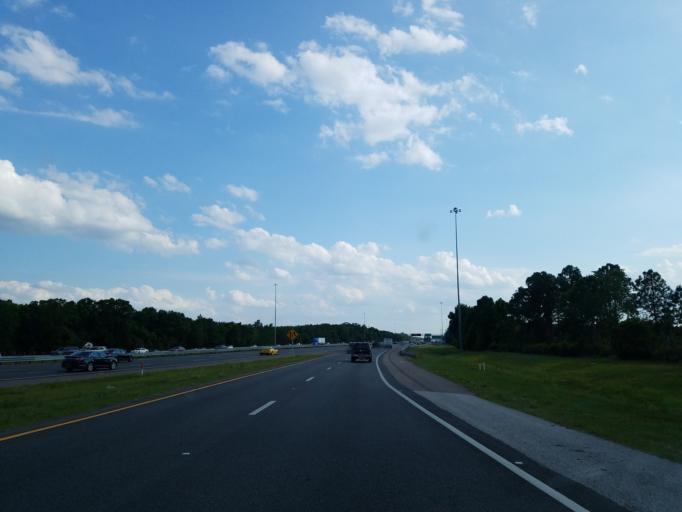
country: US
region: Florida
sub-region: Hillsborough County
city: Pebble Creek
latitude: 28.1916
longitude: -82.3860
